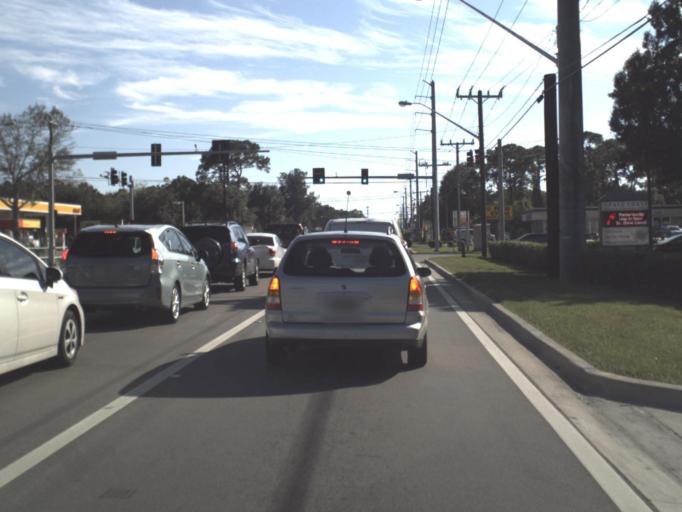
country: US
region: Florida
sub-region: Brevard County
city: June Park
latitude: 28.0896
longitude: -80.6727
